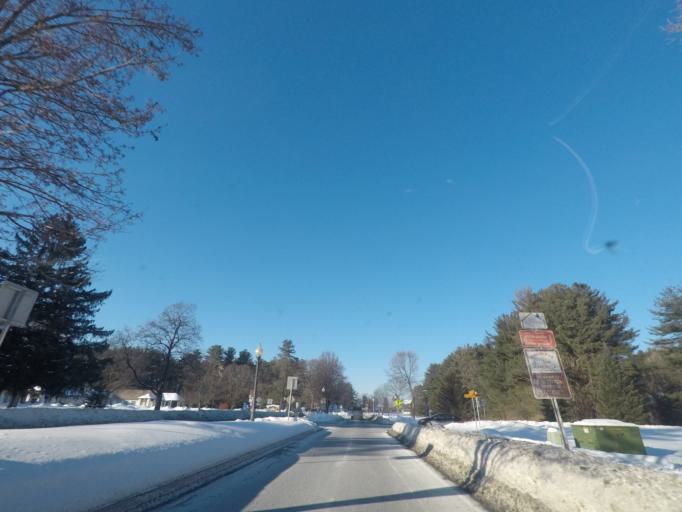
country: US
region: New York
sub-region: Saratoga County
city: Saratoga Springs
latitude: 43.0651
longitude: -73.7887
